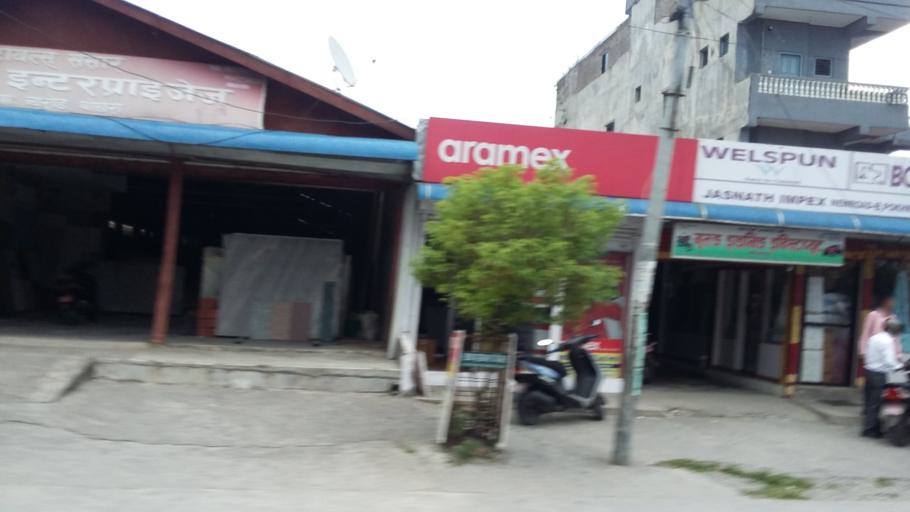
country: NP
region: Western Region
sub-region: Gandaki Zone
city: Pokhara
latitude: 28.2130
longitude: 83.9855
